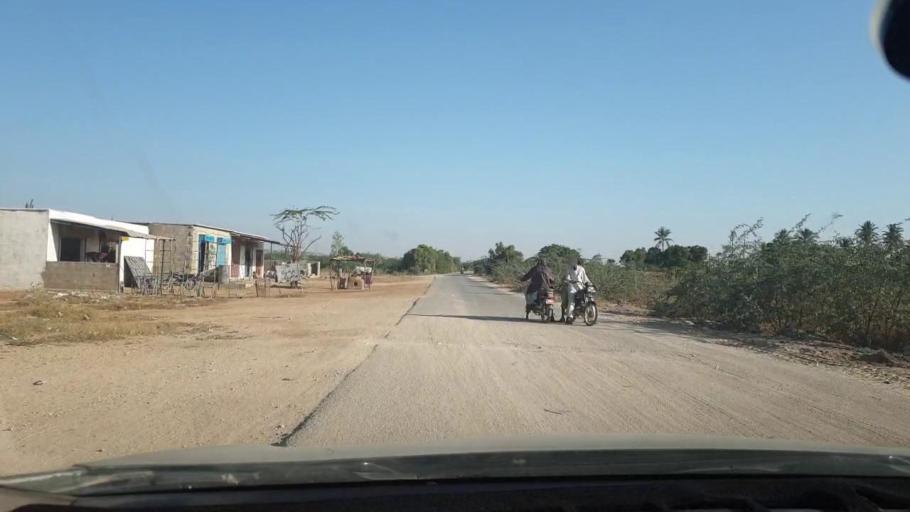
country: PK
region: Sindh
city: Malir Cantonment
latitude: 25.1730
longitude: 67.2020
